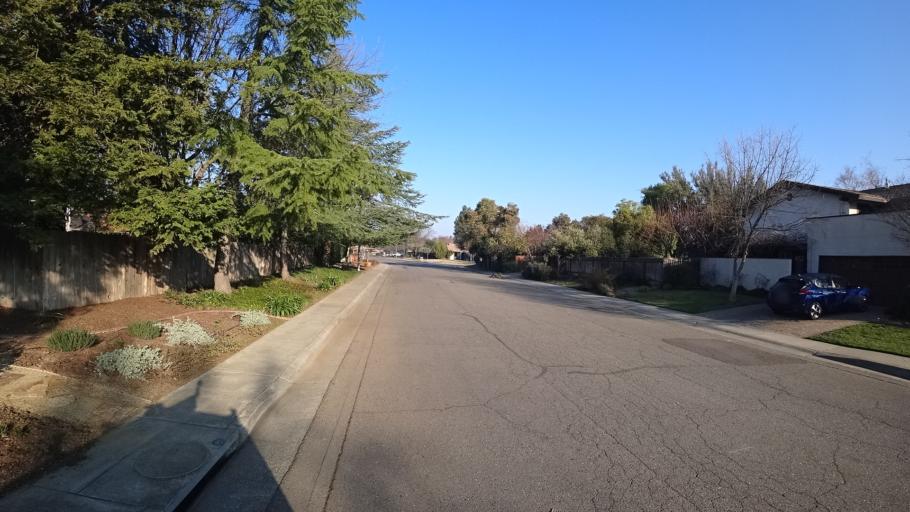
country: US
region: California
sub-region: Yolo County
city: Davis
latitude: 38.5564
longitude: -121.7912
